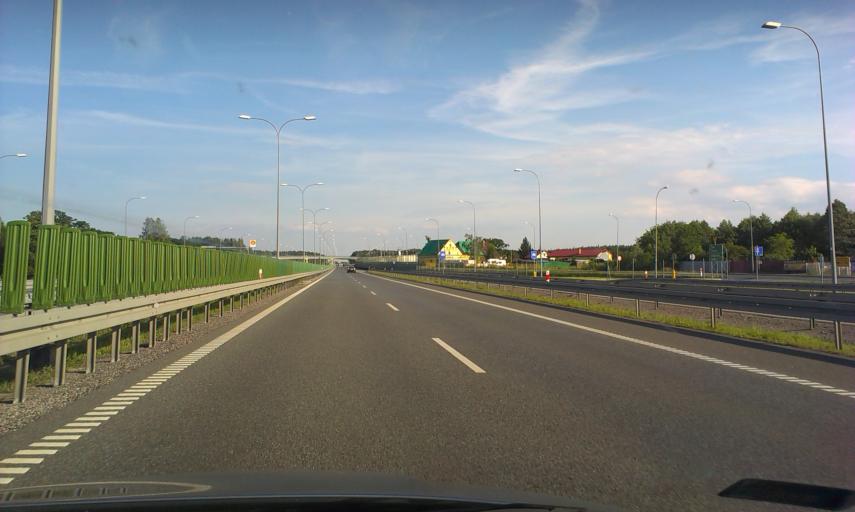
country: PL
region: Kujawsko-Pomorskie
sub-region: Powiat bydgoski
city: Biale Blota
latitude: 53.0919
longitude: 17.8994
